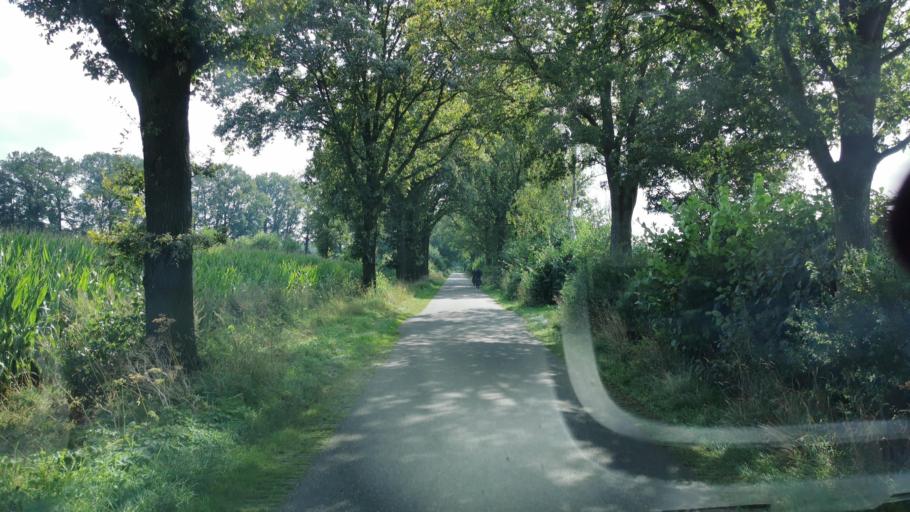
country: NL
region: Overijssel
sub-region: Gemeente Oldenzaal
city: Oldenzaal
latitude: 52.3363
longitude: 6.8453
